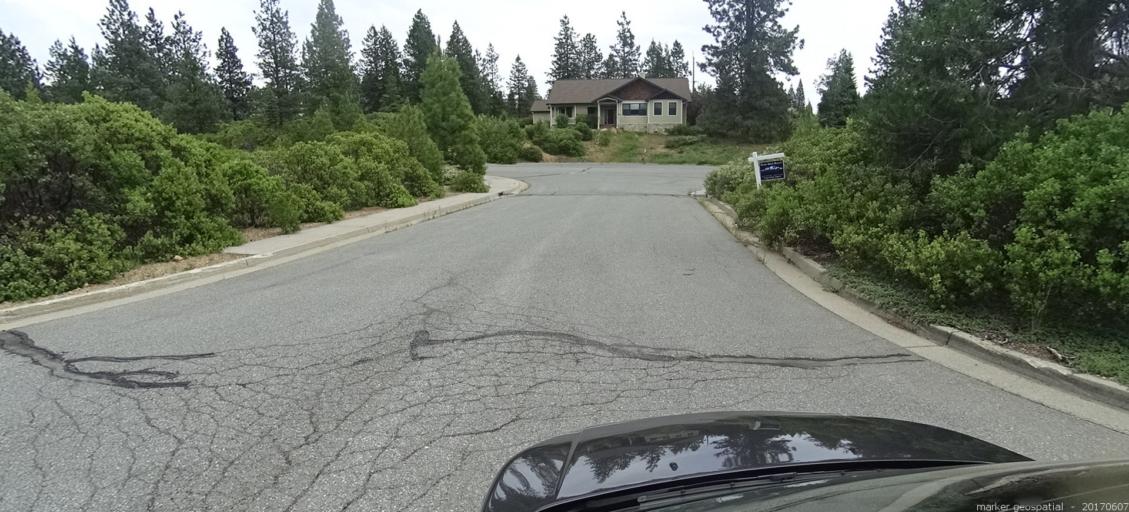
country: US
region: California
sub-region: Siskiyou County
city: Mount Shasta
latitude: 41.2880
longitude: -122.3169
